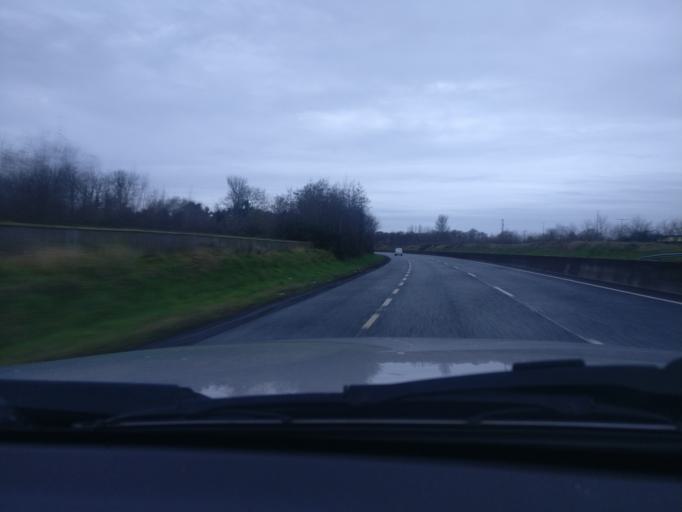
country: IE
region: Leinster
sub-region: An Mhi
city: Navan
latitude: 53.6502
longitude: -6.7086
